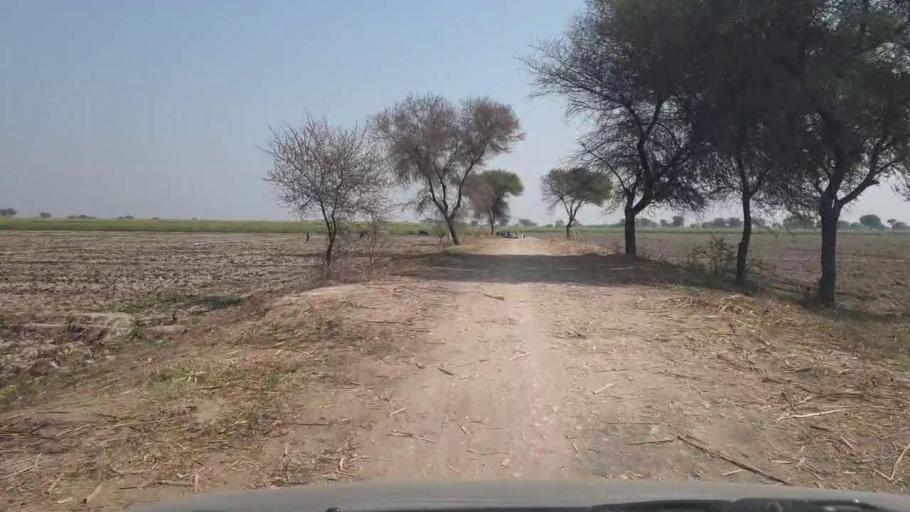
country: PK
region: Sindh
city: Mirwah Gorchani
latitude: 25.3045
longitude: 69.1576
